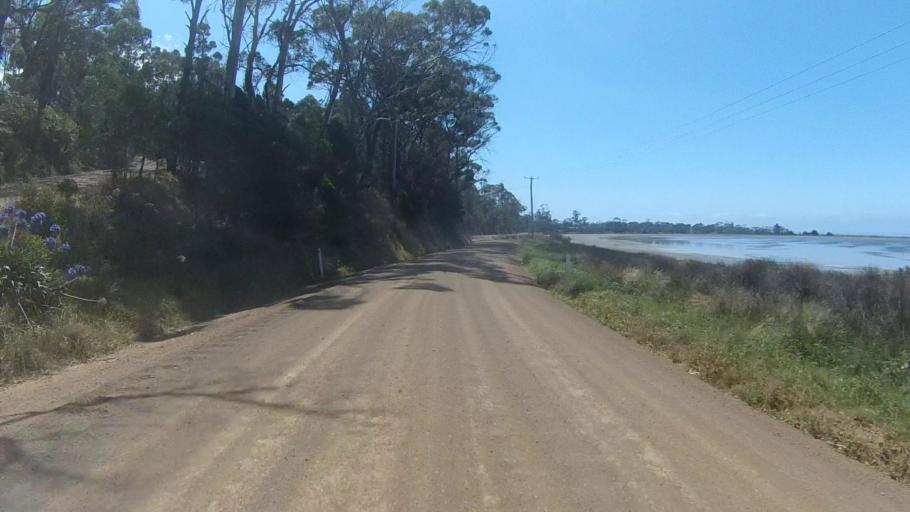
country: AU
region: Tasmania
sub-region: Sorell
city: Sorell
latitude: -42.8506
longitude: 147.8403
